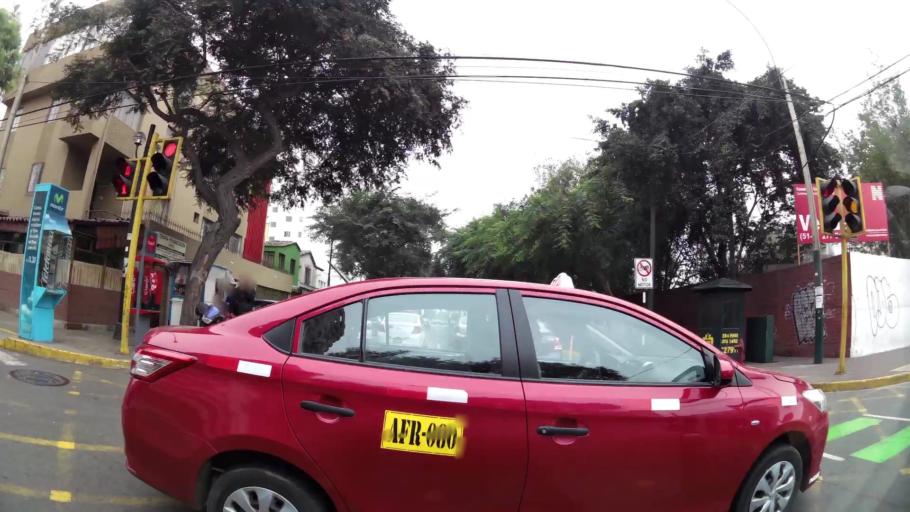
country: PE
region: Lima
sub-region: Lima
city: San Isidro
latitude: -12.0909
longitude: -77.0347
